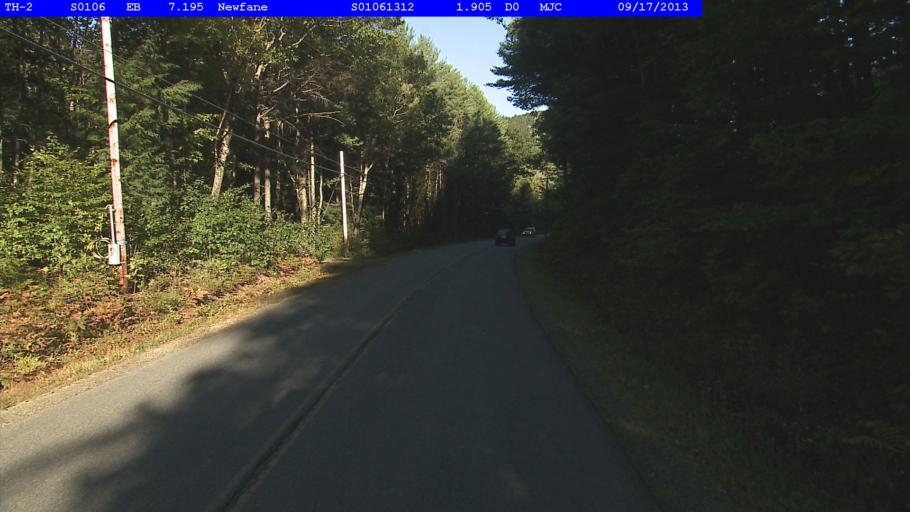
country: US
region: Vermont
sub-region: Windham County
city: Dover
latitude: 42.9462
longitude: -72.7332
